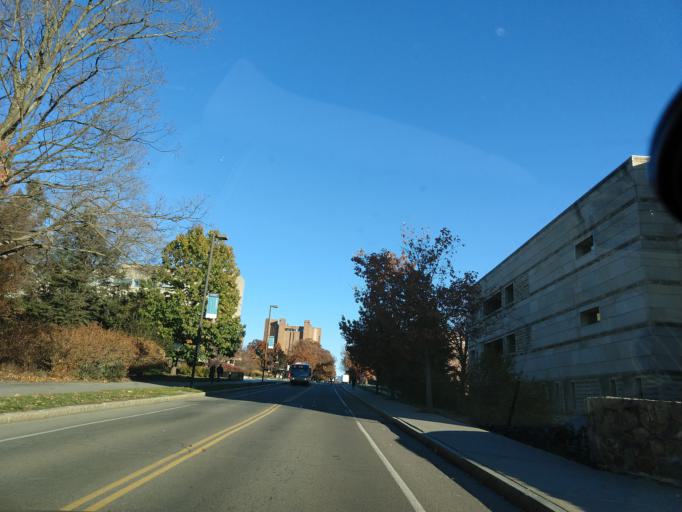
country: US
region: New York
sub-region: Tompkins County
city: East Ithaca
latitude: 42.4476
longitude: -76.4810
